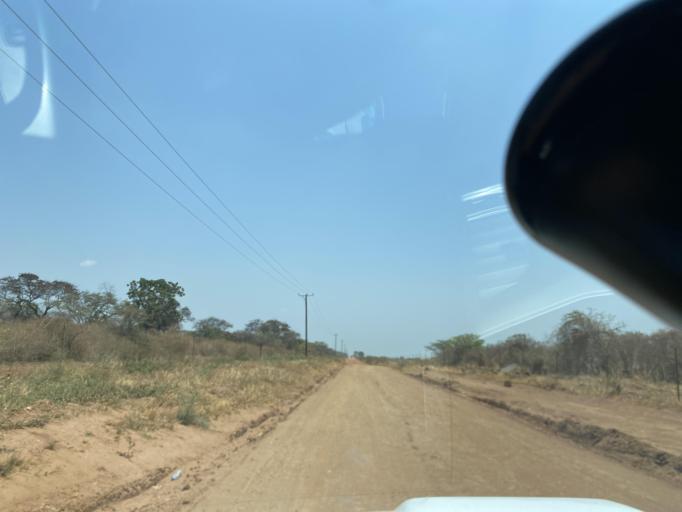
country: ZM
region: Lusaka
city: Lusaka
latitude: -15.4355
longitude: 28.0744
